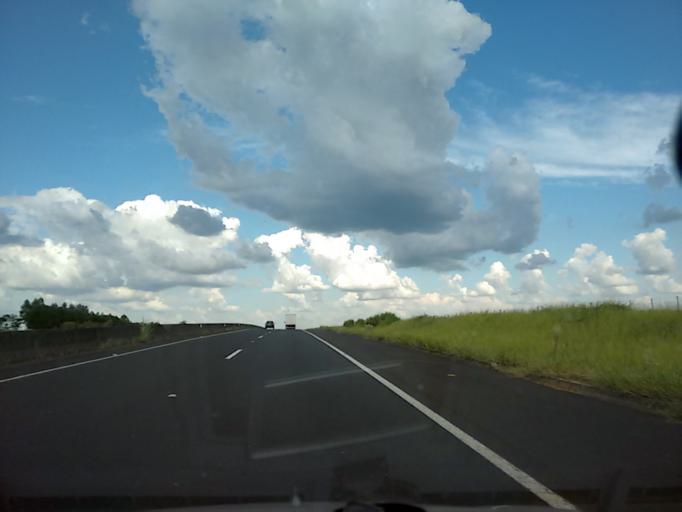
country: BR
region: Sao Paulo
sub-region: Garca
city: Garca
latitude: -22.2265
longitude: -49.7889
